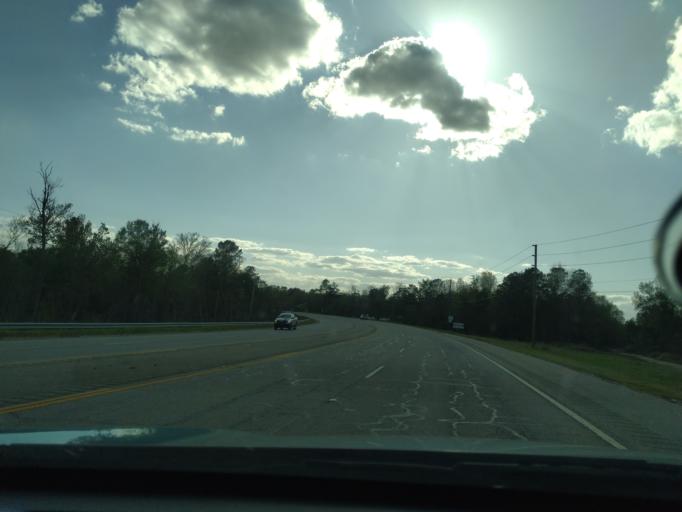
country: US
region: South Carolina
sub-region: Williamsburg County
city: Kingstree
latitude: 33.6577
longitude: -79.8738
